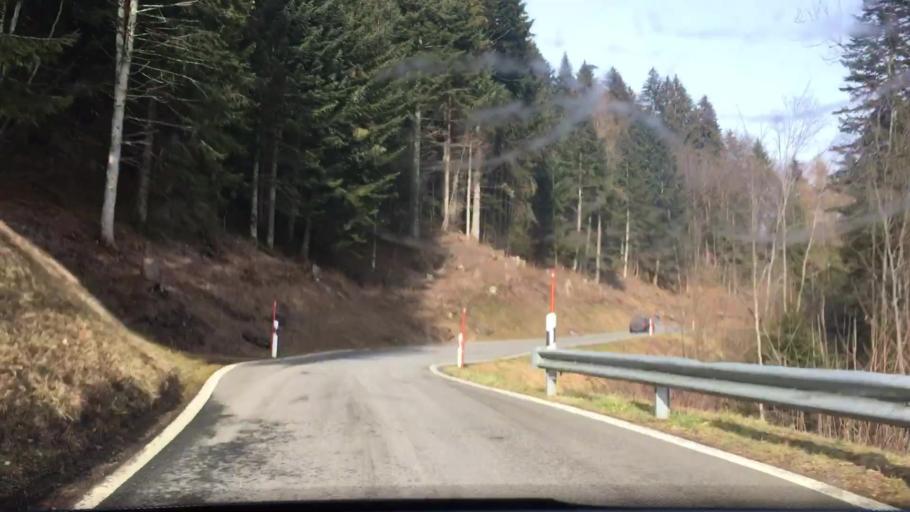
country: CH
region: Valais
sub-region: Monthey District
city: Troistorrents
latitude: 46.2233
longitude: 6.8995
